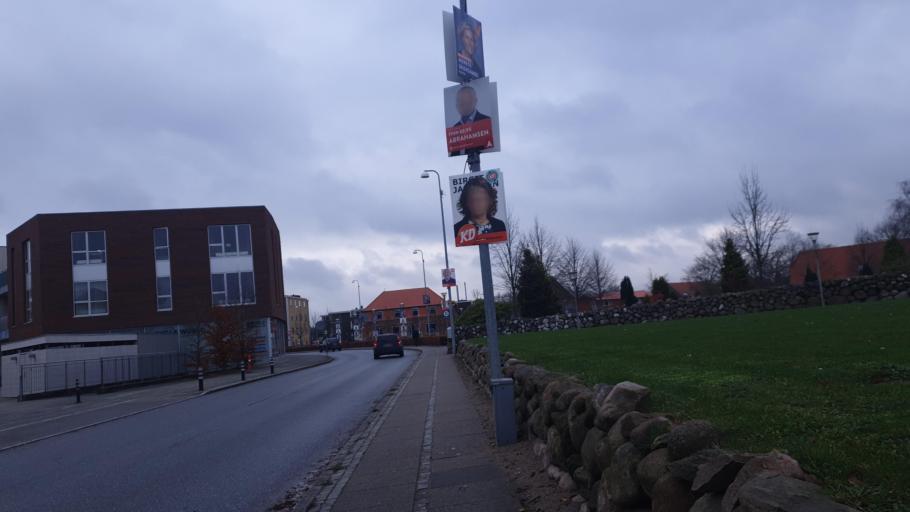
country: DK
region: Central Jutland
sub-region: Hedensted Kommune
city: Hedensted
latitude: 55.7695
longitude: 9.7024
